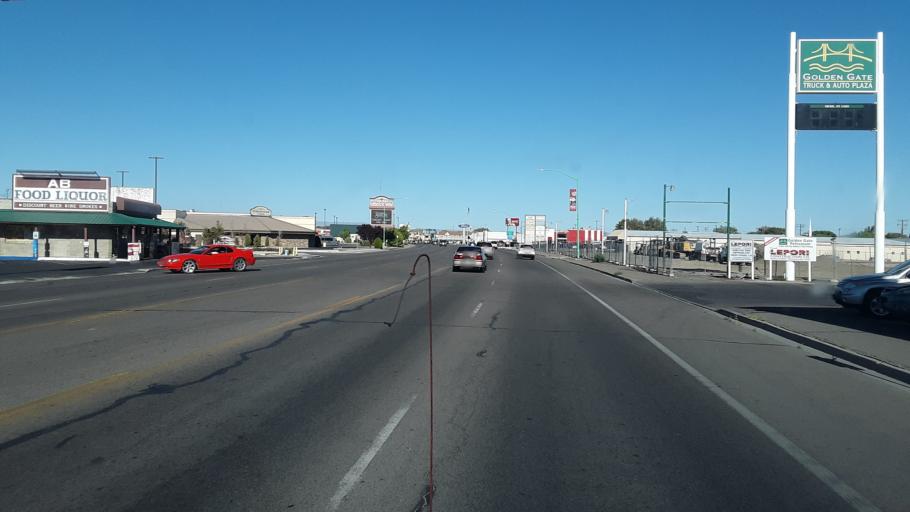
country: US
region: Nevada
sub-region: Churchill County
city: Fallon
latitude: 39.4752
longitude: -118.7965
